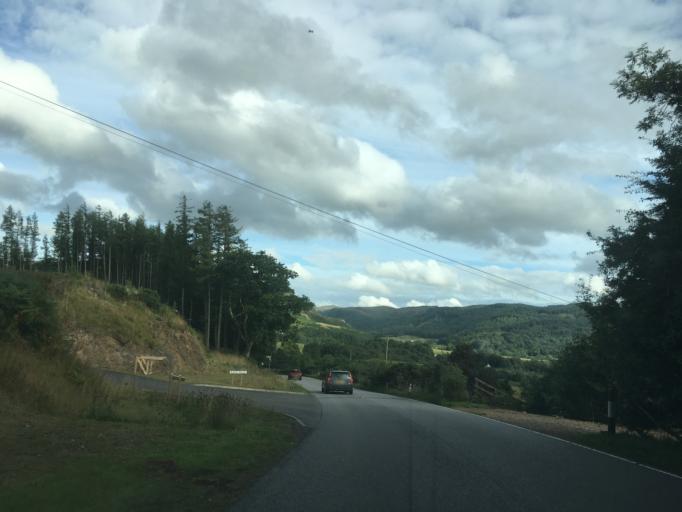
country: GB
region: Scotland
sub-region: Argyll and Bute
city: Oban
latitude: 56.3766
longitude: -5.4486
